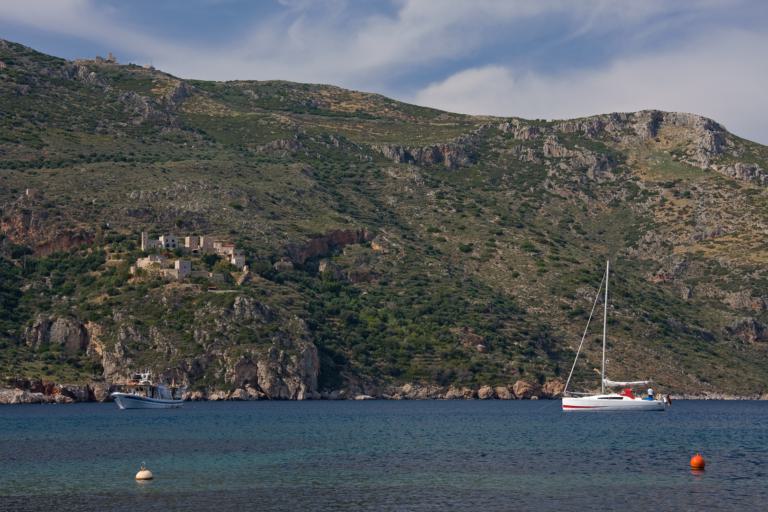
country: GR
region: Peloponnese
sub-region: Nomos Lakonias
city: Gytheio
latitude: 36.4279
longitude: 22.4858
